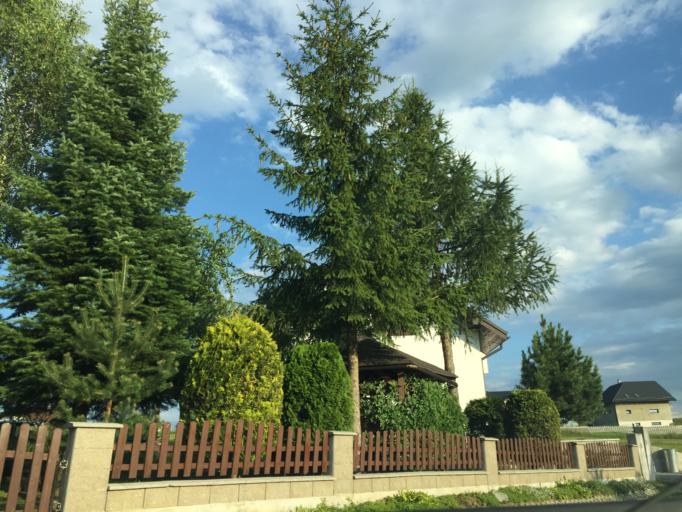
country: PL
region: Silesian Voivodeship
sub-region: Powiat zywiecki
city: Korbielow
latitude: 49.4606
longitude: 19.3179
